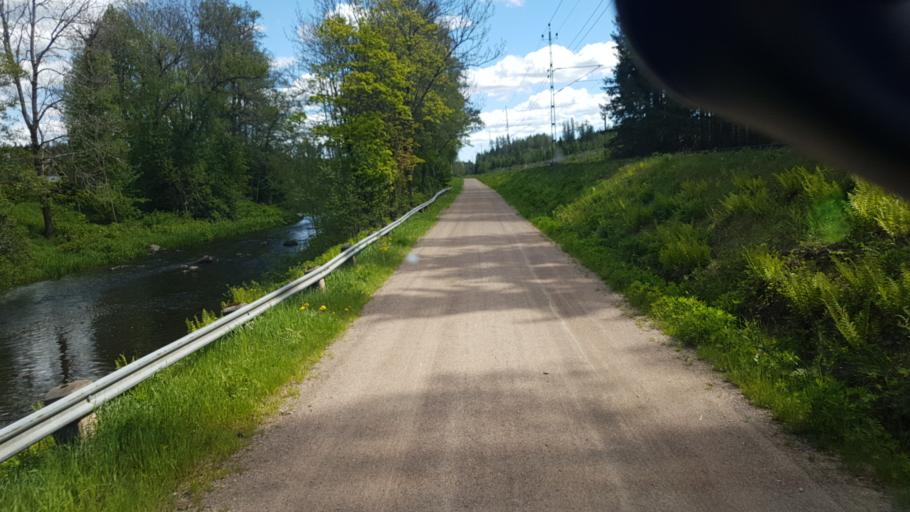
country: SE
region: Vaermland
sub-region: Sunne Kommun
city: Sunne
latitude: 59.6173
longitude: 12.9626
